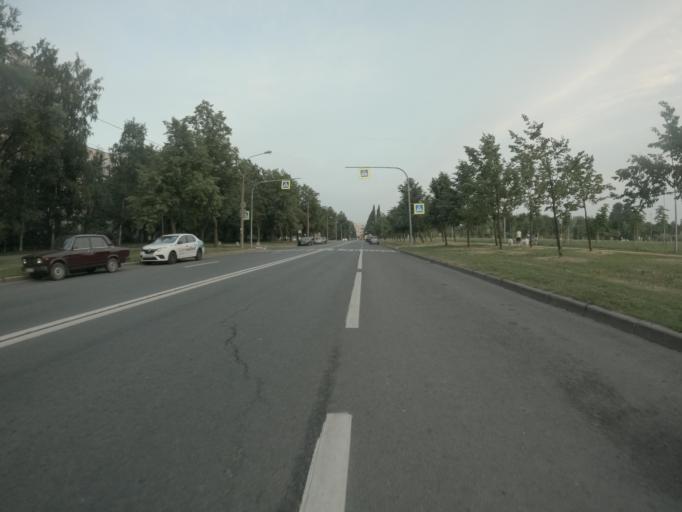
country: RU
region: St.-Petersburg
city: Krasnogvargeisky
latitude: 59.9645
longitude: 30.4312
